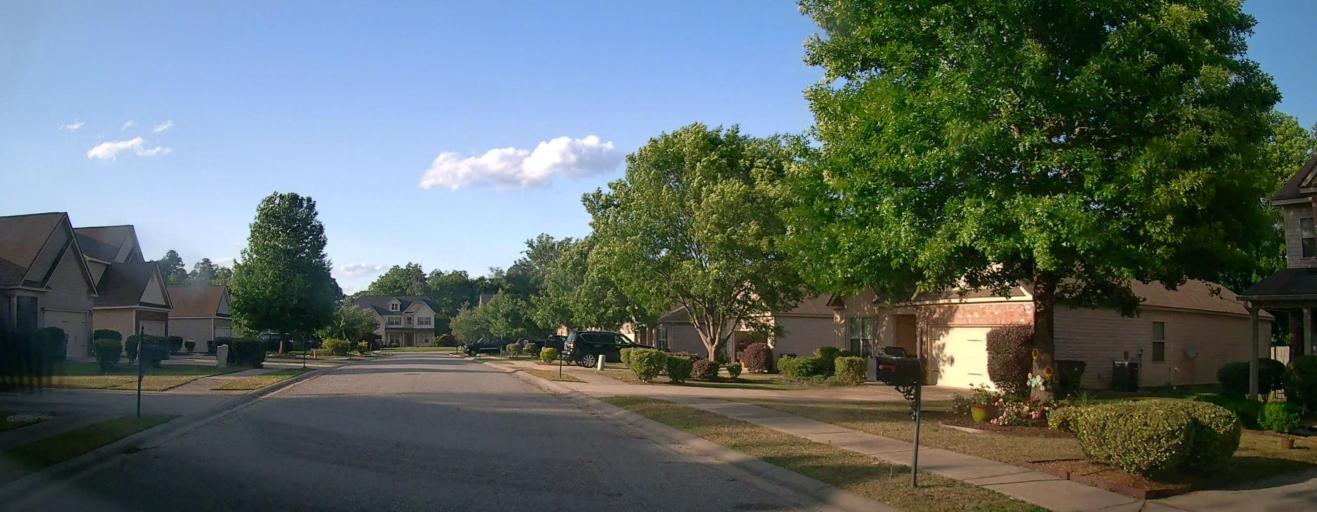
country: US
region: Georgia
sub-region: Peach County
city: Byron
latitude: 32.6400
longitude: -83.7586
